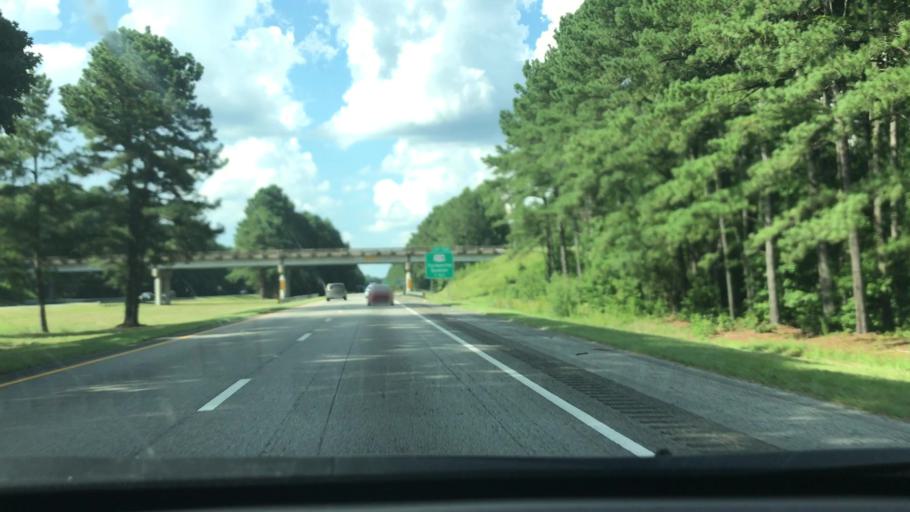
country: US
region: South Carolina
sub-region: Sumter County
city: East Sumter
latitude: 33.8851
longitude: -80.0994
